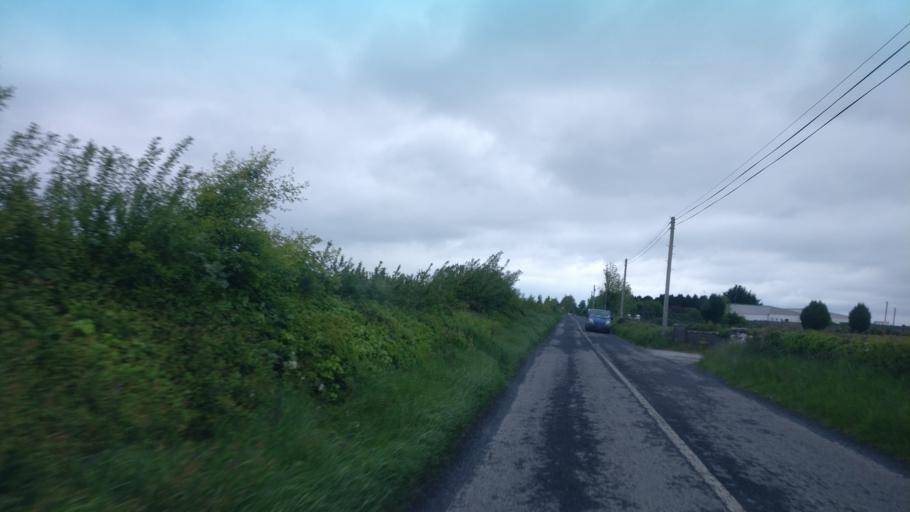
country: IE
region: Connaught
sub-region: County Galway
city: Portumna
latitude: 53.1114
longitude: -8.2745
